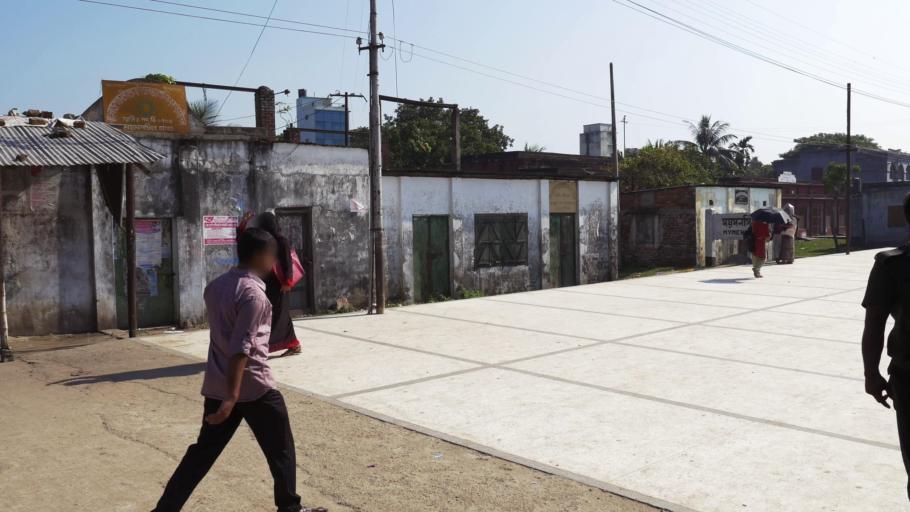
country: BD
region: Dhaka
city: Mymensingh
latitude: 24.6979
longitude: 90.4508
